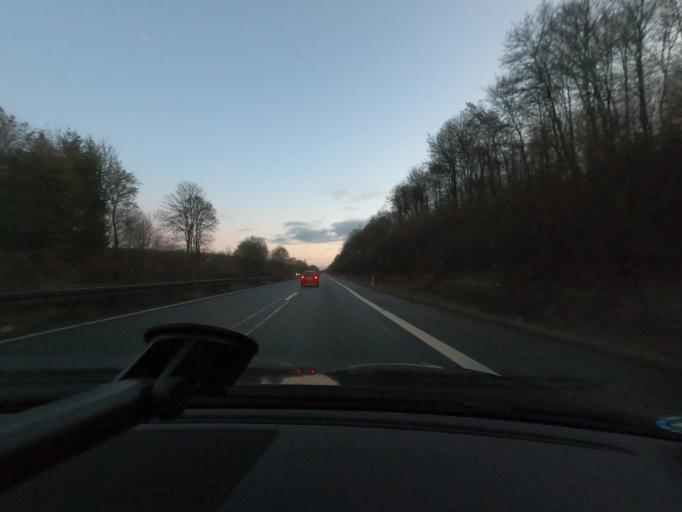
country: DE
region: Lower Saxony
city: Hoerden
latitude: 51.7046
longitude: 10.2797
